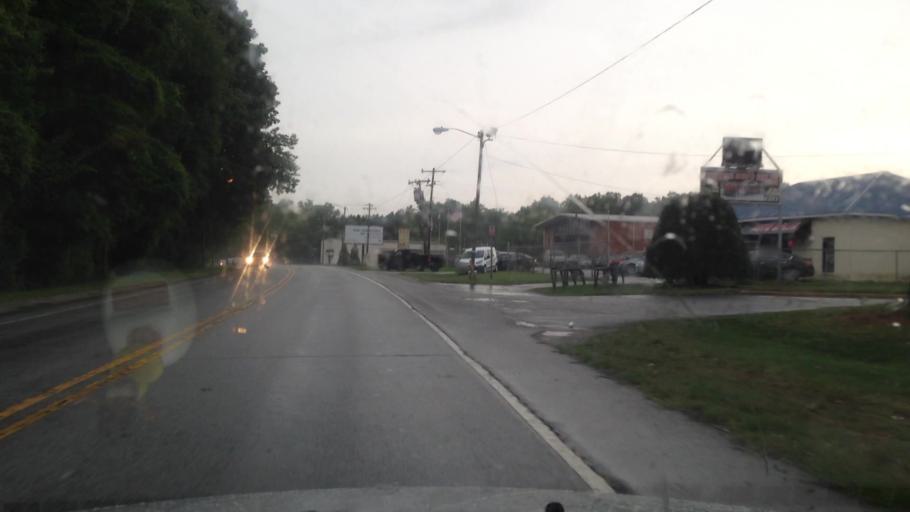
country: US
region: North Carolina
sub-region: Guilford County
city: Greensboro
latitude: 36.0539
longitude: -79.8578
